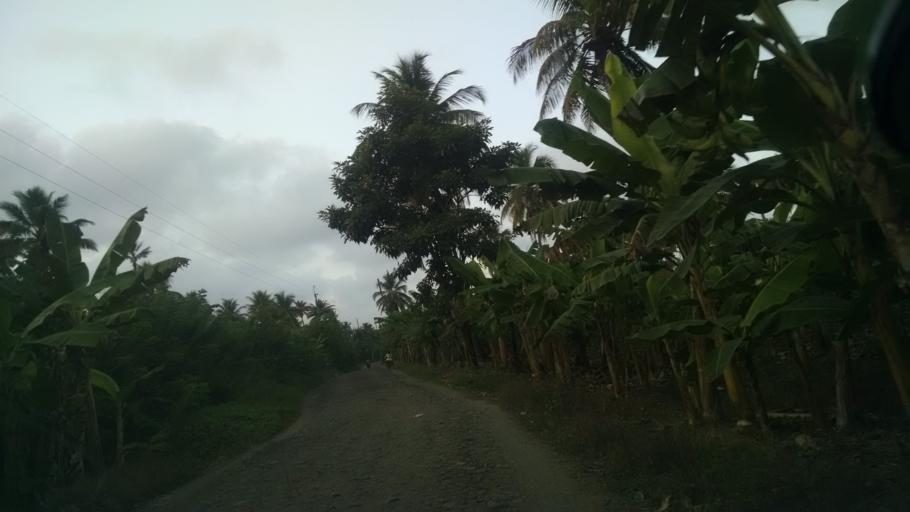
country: CO
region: Antioquia
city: San Juan de Uraba
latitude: 8.7340
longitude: -76.6060
